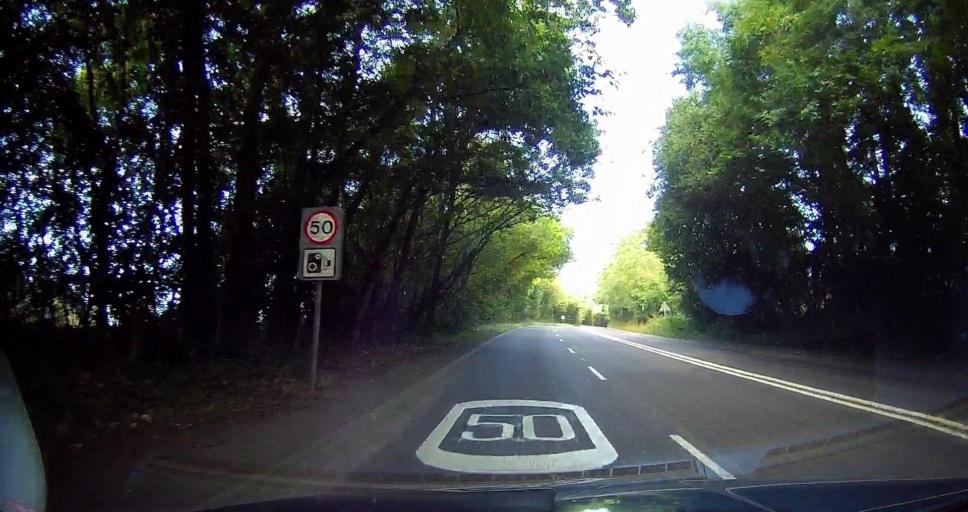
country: GB
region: England
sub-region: Kent
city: East Peckham
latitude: 51.2409
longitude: 0.3775
